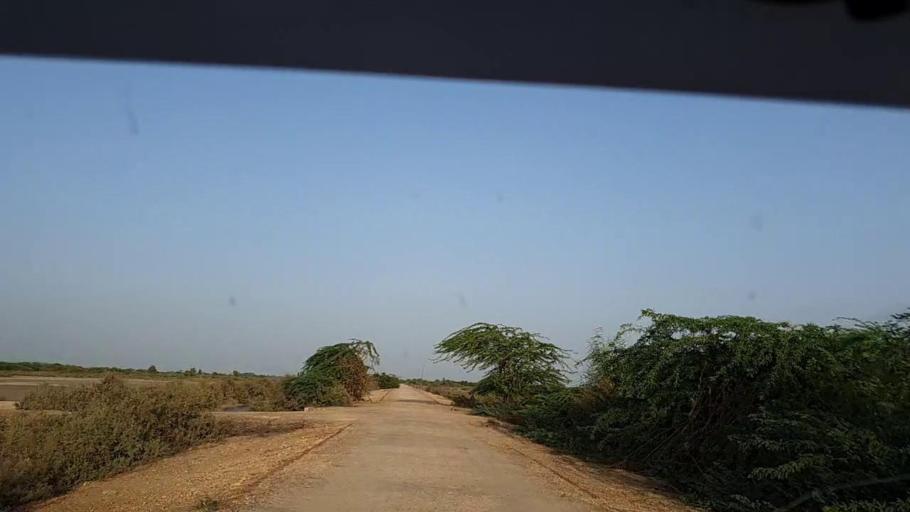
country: PK
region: Sindh
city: Kadhan
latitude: 24.5469
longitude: 68.9436
